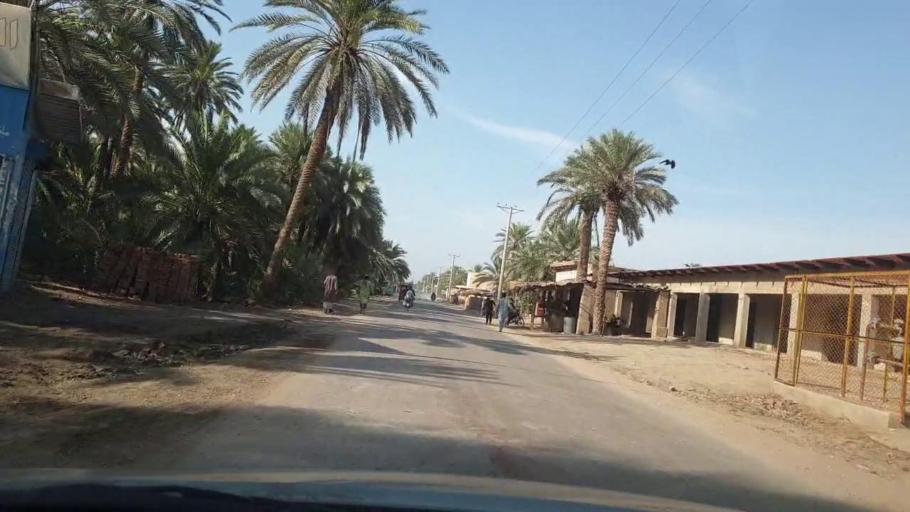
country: PK
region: Sindh
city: Sukkur
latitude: 27.6573
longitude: 68.8412
